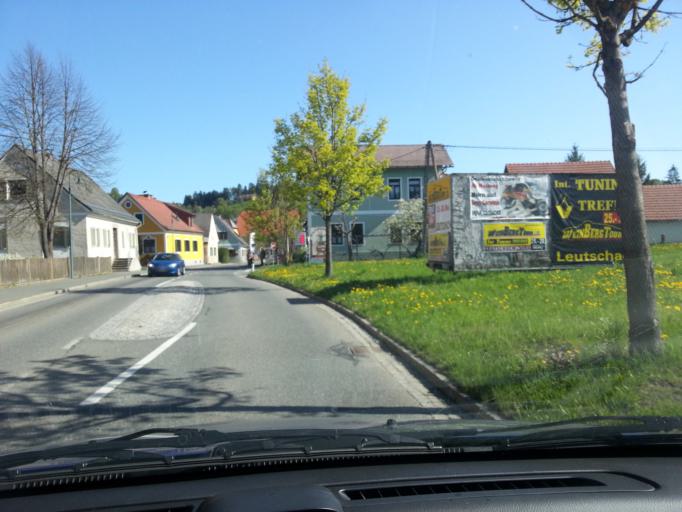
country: AT
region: Styria
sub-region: Politischer Bezirk Leibnitz
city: Leutschach
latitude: 46.6627
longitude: 15.4698
